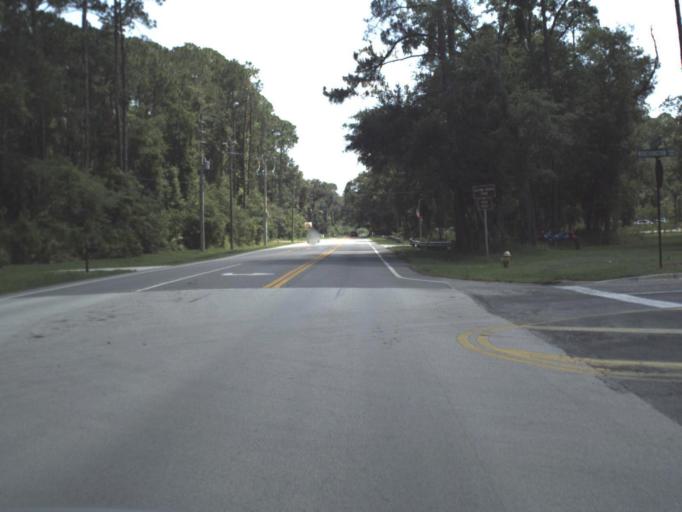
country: US
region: Florida
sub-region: Saint Johns County
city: Fruit Cove
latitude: 30.0743
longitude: -81.6495
